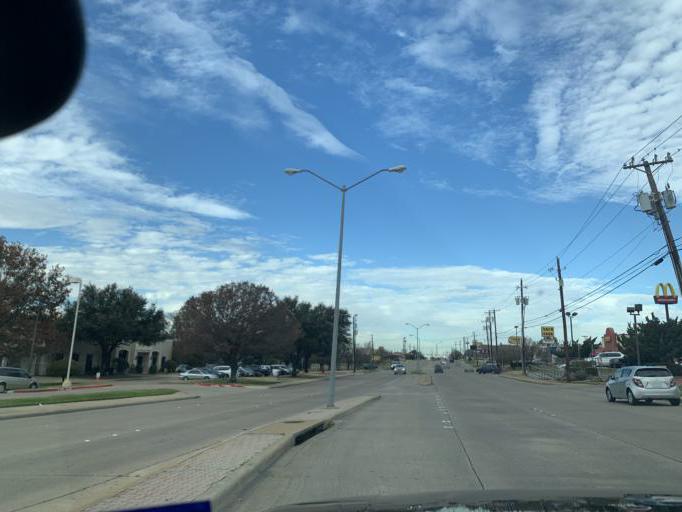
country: US
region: Texas
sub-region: Dallas County
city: Duncanville
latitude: 32.6431
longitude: -96.8914
